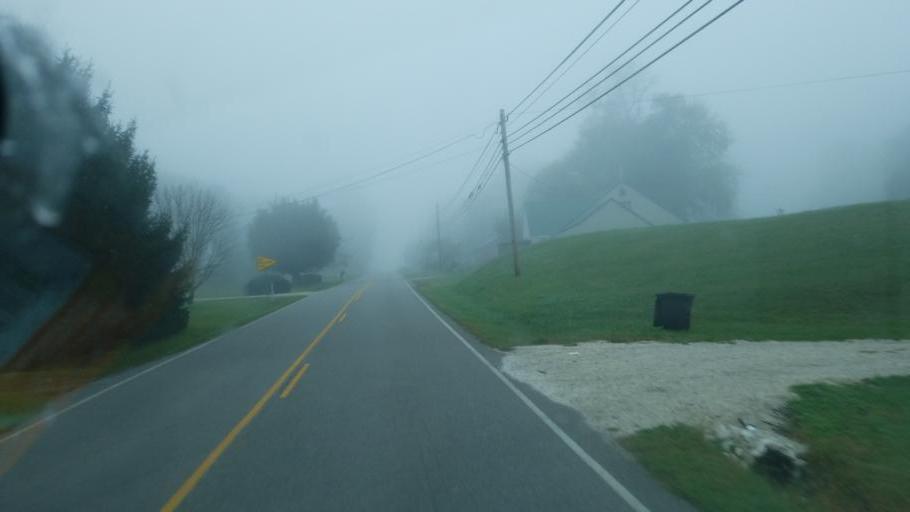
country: US
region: Ohio
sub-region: Scioto County
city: Portsmouth
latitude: 38.7161
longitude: -83.0222
